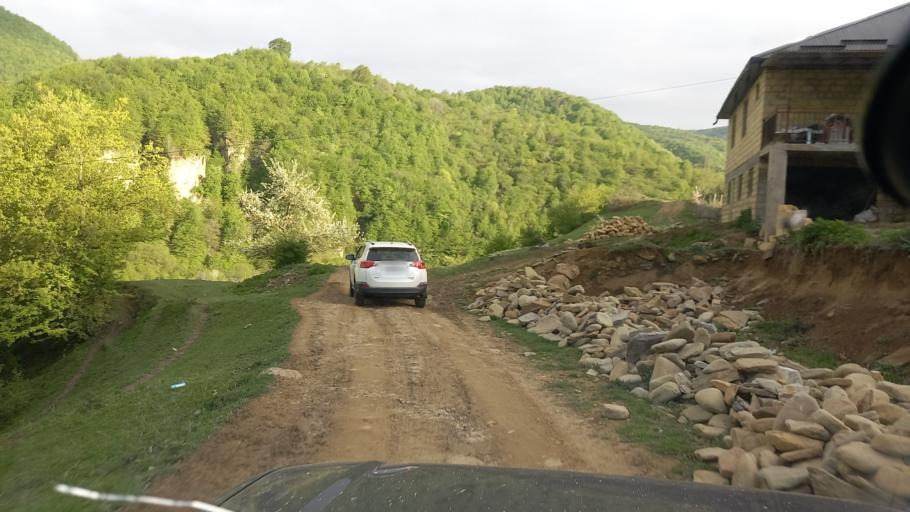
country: RU
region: Dagestan
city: Khuchni
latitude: 41.9470
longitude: 47.8340
